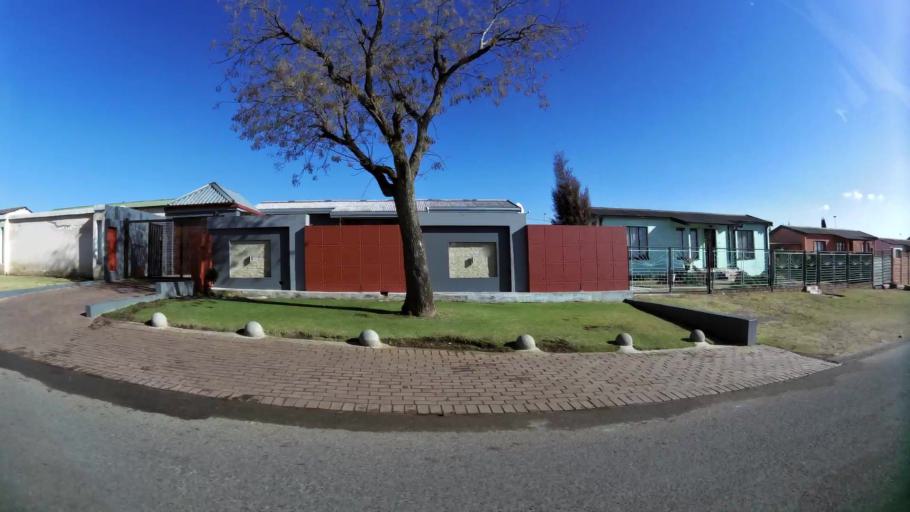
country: ZA
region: Gauteng
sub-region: City of Johannesburg Metropolitan Municipality
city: Roodepoort
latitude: -26.2203
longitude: 27.9185
